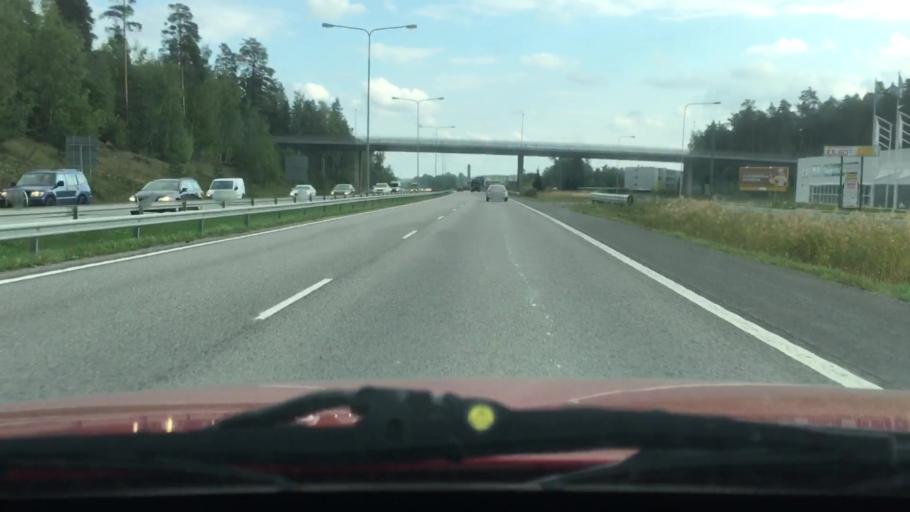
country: FI
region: Varsinais-Suomi
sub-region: Turku
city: Raisio
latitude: 60.4971
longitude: 22.1640
